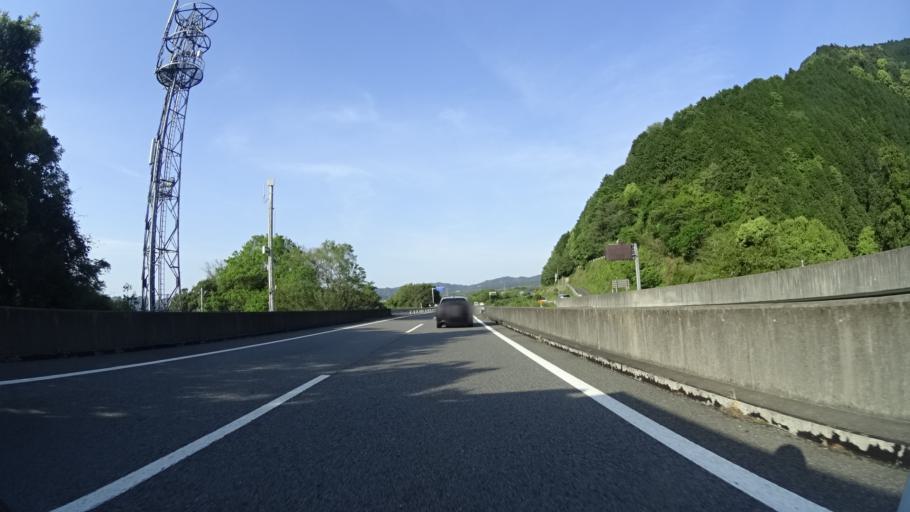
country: JP
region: Ehime
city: Niihama
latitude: 33.9231
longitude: 133.3181
